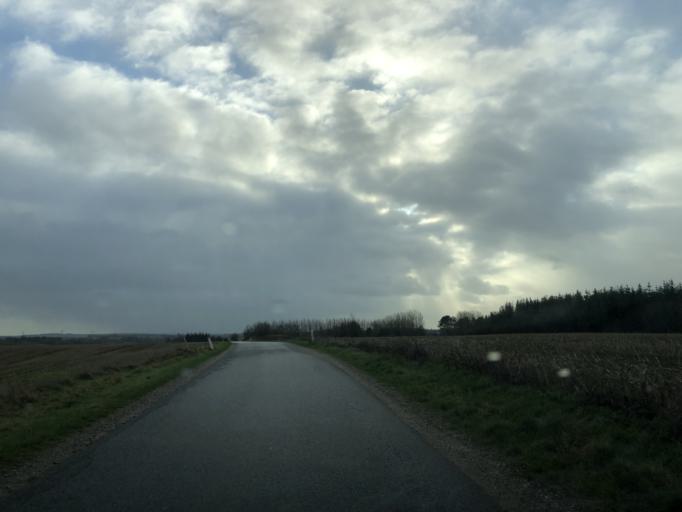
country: DK
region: North Denmark
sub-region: Rebild Kommune
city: Stovring
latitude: 56.9115
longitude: 9.7796
